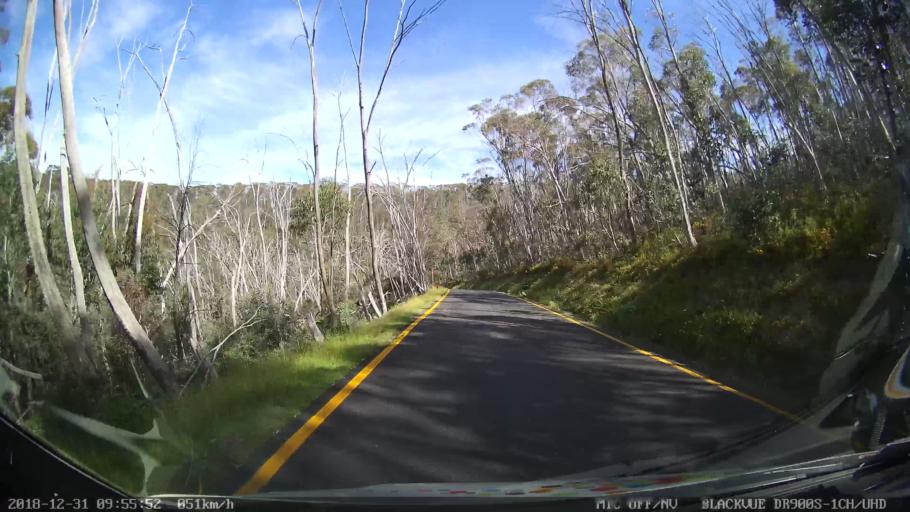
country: AU
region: New South Wales
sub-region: Snowy River
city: Jindabyne
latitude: -36.5312
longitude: 148.2274
